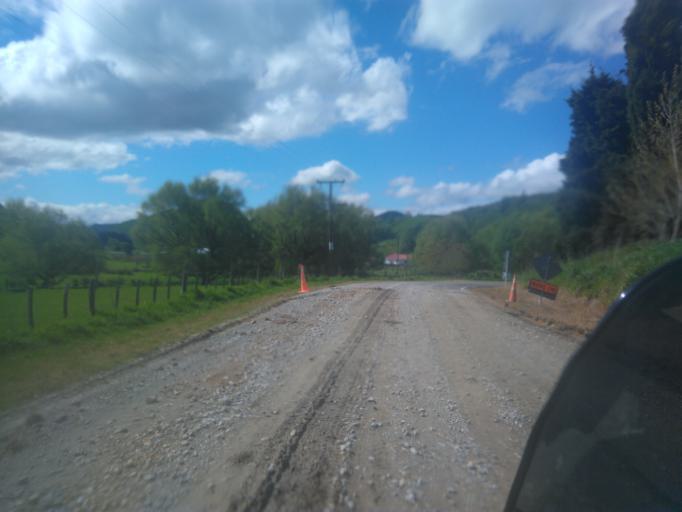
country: NZ
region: Gisborne
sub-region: Gisborne District
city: Gisborne
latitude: -38.6920
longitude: 177.7293
